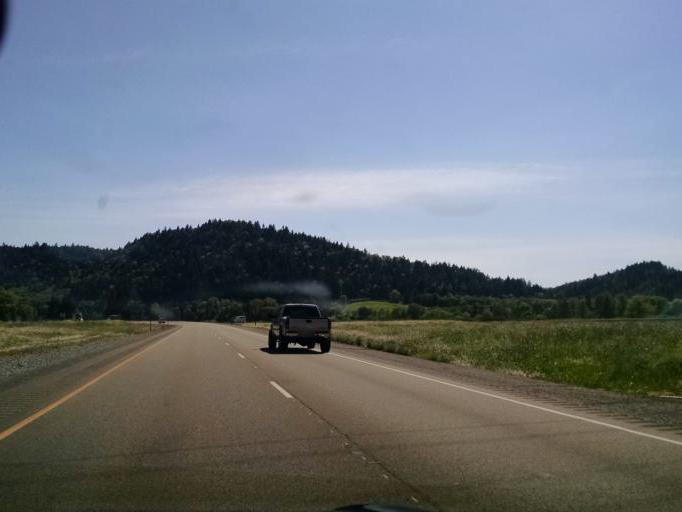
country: US
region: Oregon
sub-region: Douglas County
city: Tri-City
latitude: 42.9733
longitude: -123.3363
